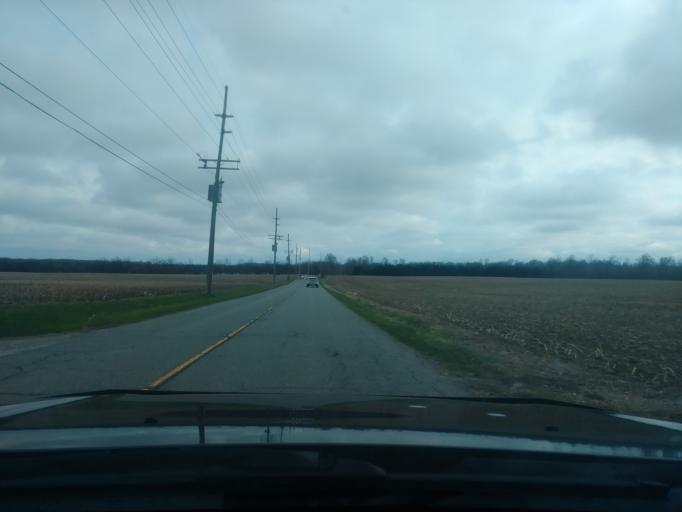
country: US
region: Indiana
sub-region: LaPorte County
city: LaPorte
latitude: 41.6411
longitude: -86.7985
